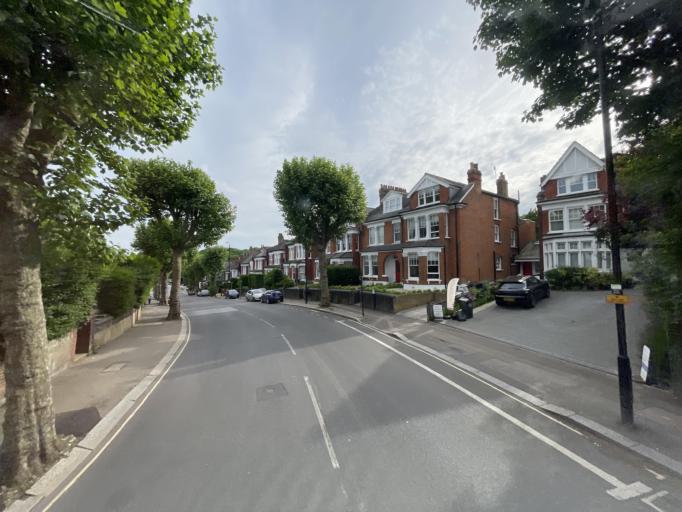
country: GB
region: England
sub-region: Greater London
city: Crouch End
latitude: 51.5882
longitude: -0.1467
